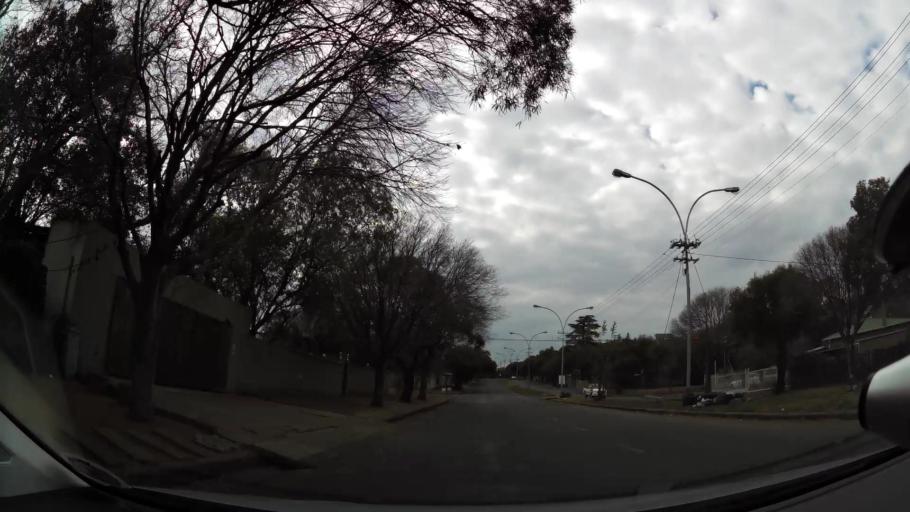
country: ZA
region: Orange Free State
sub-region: Mangaung Metropolitan Municipality
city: Bloemfontein
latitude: -29.0997
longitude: 26.2082
